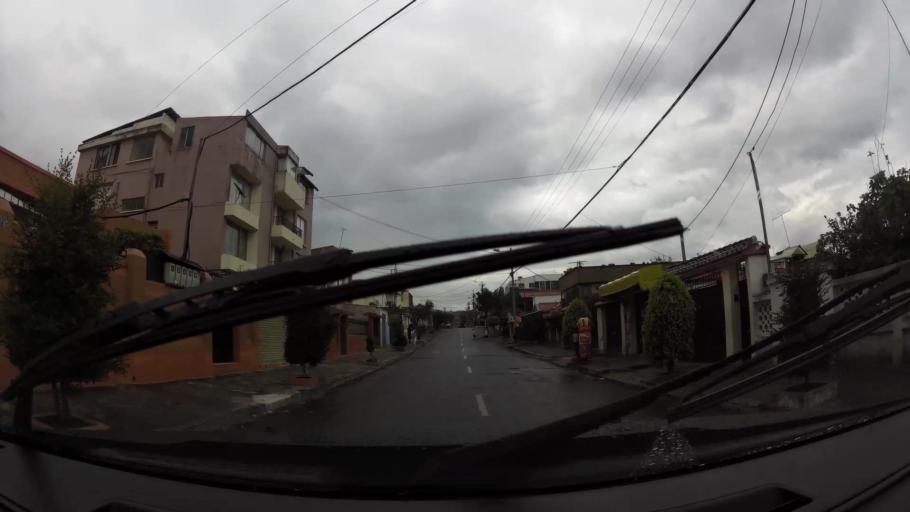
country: EC
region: Pichincha
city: Quito
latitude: -0.1962
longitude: -78.5090
